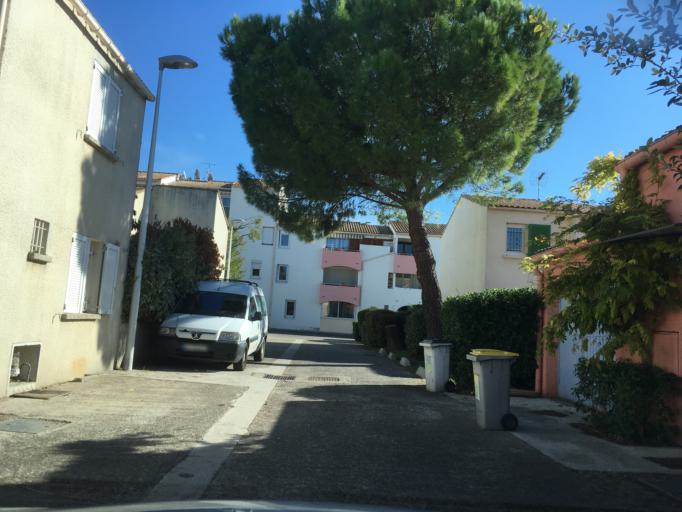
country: FR
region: Languedoc-Roussillon
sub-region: Departement de l'Herault
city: Saint-Jean-de-Vedas
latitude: 43.5980
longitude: 3.8365
